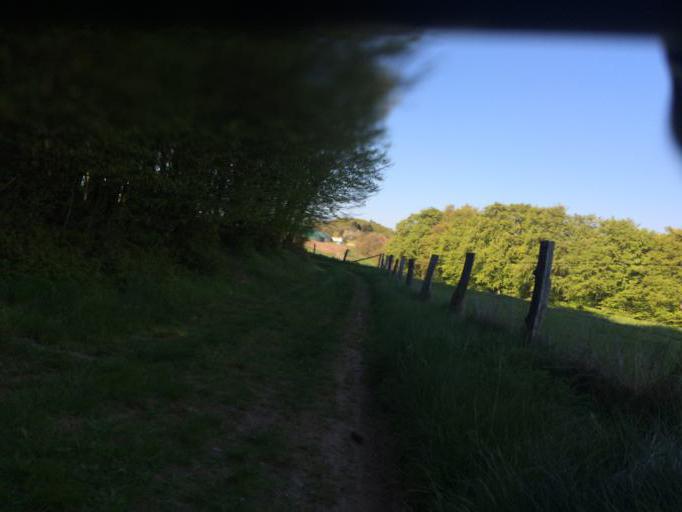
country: DE
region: Hesse
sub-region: Regierungsbezirk Kassel
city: Vohl
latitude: 51.1676
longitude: 8.8407
